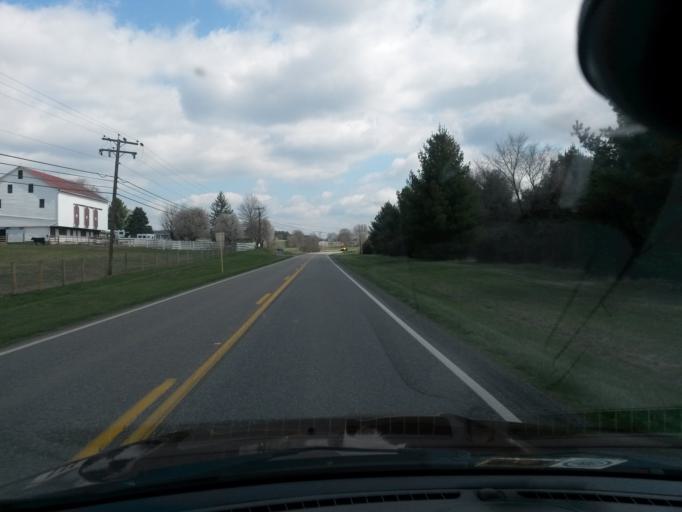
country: US
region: Virginia
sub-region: Rockingham County
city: Massanetta Springs
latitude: 38.3415
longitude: -78.8585
